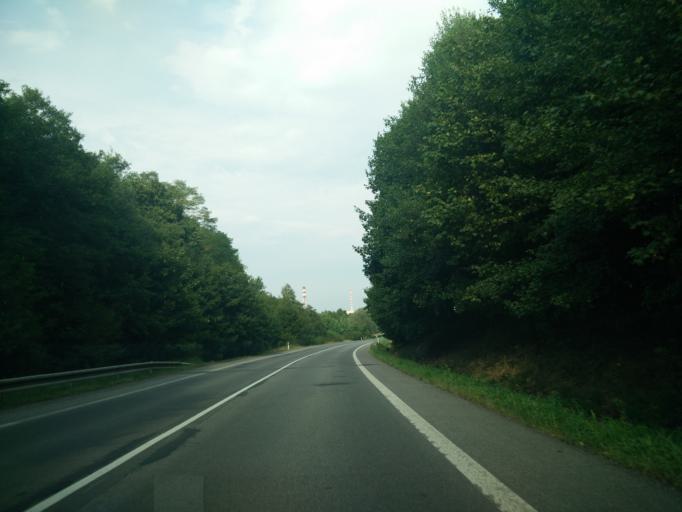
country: SK
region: Banskobystricky
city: Ziar nad Hronom
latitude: 48.5583
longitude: 18.8313
